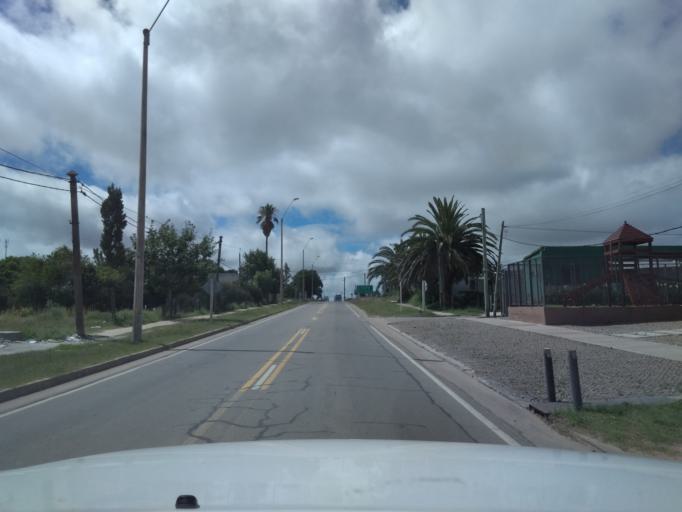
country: UY
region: Canelones
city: Pando
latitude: -34.7111
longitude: -55.9640
